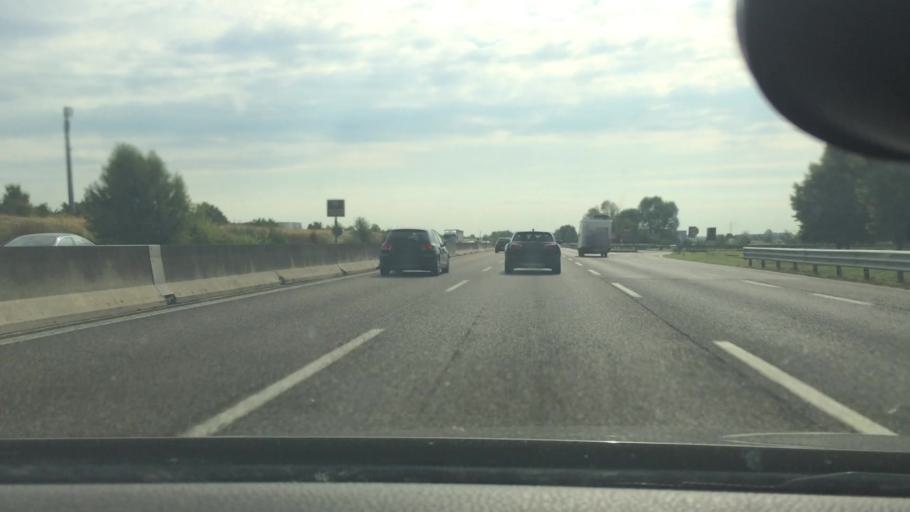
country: IT
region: Emilia-Romagna
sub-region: Provincia di Parma
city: Fontanellato
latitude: 44.8767
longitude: 10.1691
